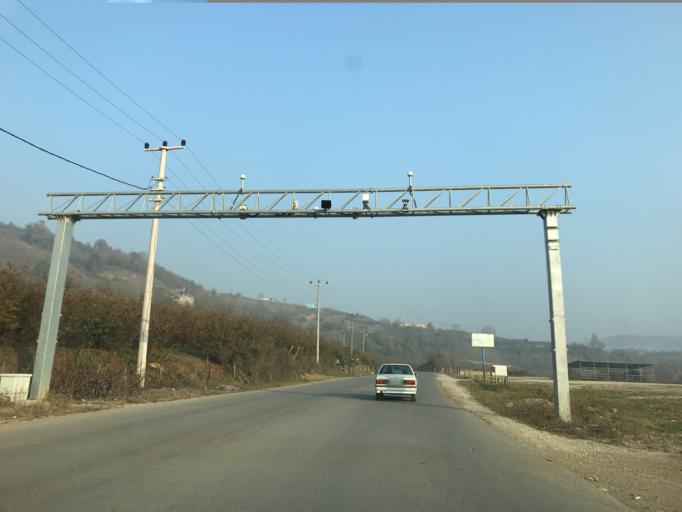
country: TR
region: Duzce
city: Cumayeri
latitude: 40.8864
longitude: 30.9522
